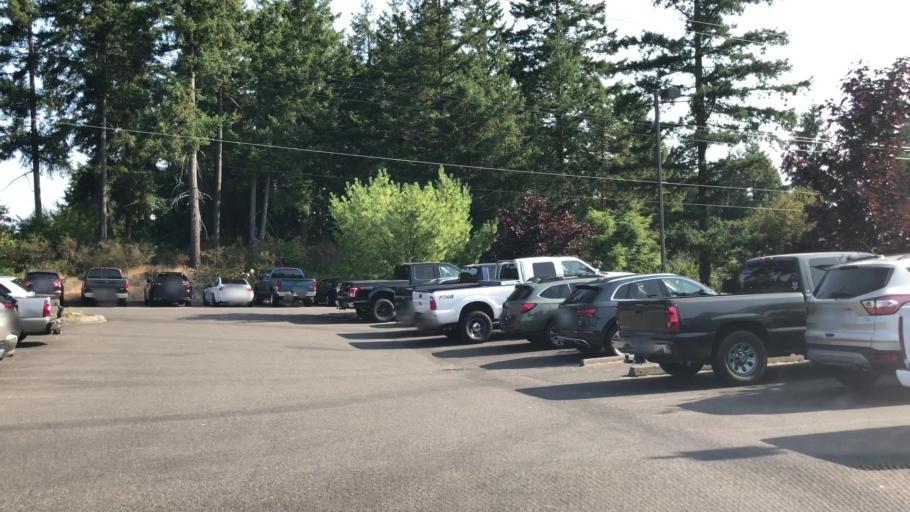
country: US
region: Washington
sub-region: Thurston County
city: Tanglewilde-Thompson Place
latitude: 47.0973
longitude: -122.7610
